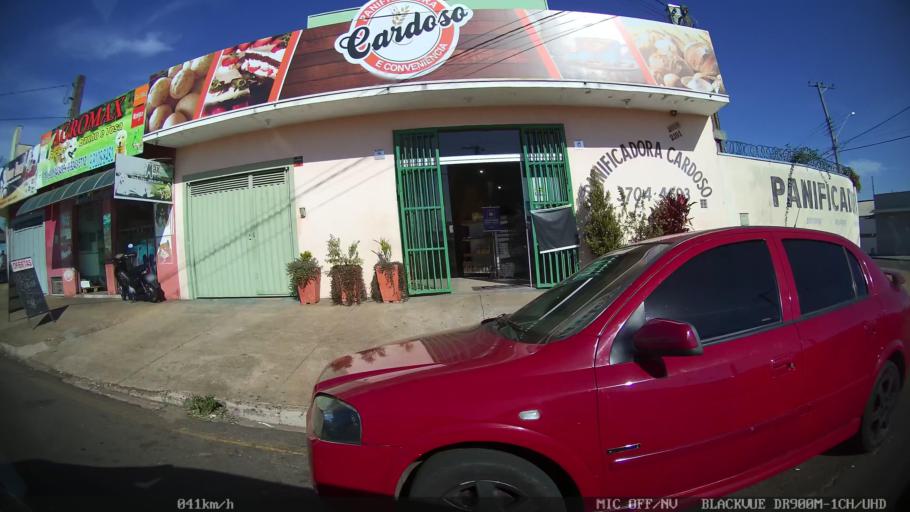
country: BR
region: Sao Paulo
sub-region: Franca
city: Franca
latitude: -20.4892
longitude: -47.4241
